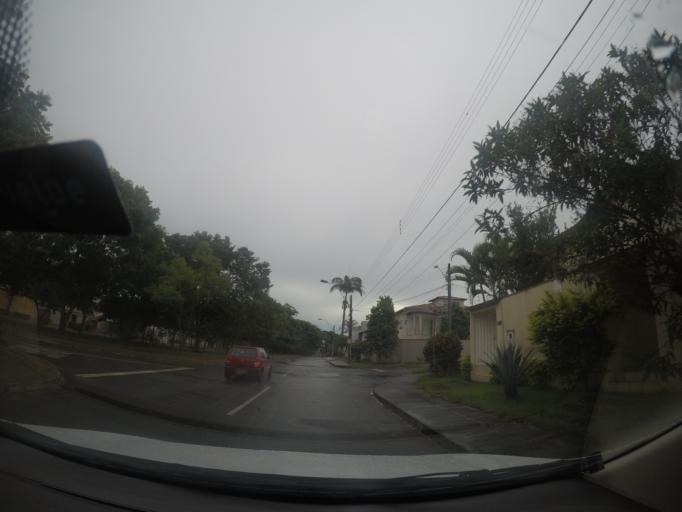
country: BR
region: Goias
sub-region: Goiania
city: Goiania
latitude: -16.6376
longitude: -49.2314
